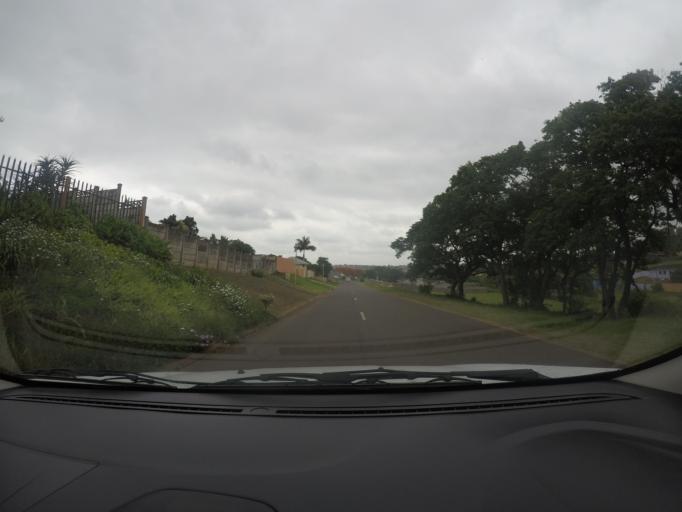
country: ZA
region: KwaZulu-Natal
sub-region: uThungulu District Municipality
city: Empangeni
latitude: -28.7599
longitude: 31.8859
